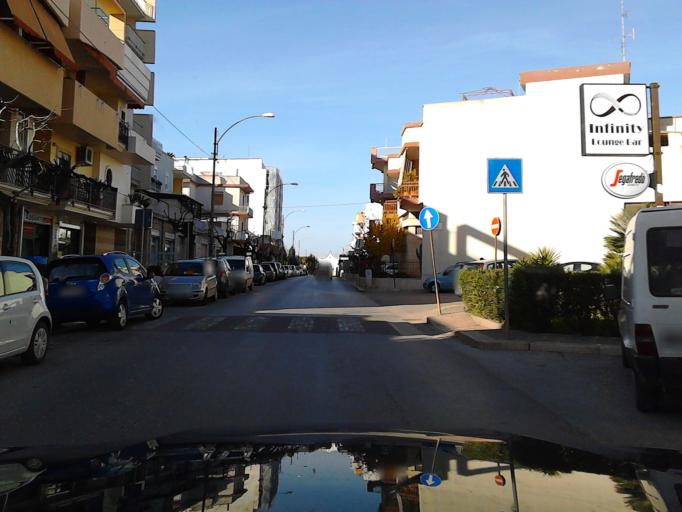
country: IT
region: Apulia
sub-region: Provincia di Bari
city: Rutigliano
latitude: 41.0158
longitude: 17.0006
